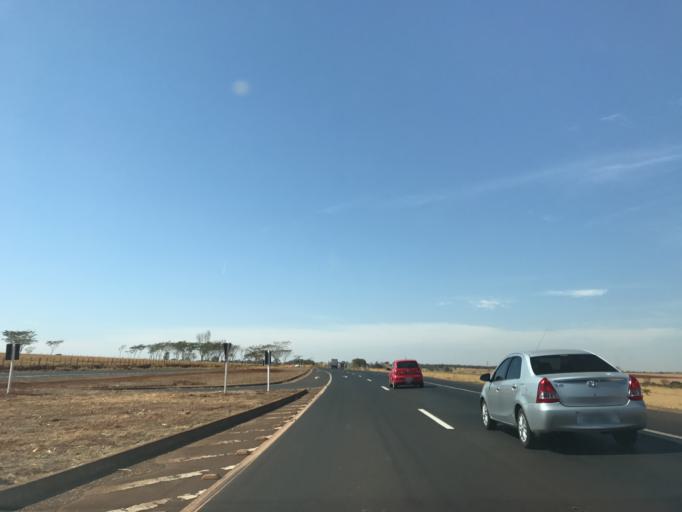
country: BR
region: Minas Gerais
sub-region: Centralina
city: Centralina
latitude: -18.6397
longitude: -49.1789
